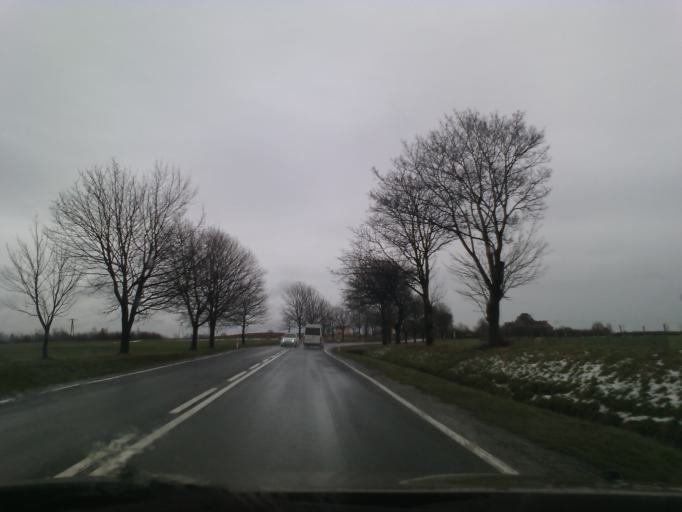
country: PL
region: Lower Silesian Voivodeship
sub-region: Powiat swidnicki
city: Swiebodzice
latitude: 50.8537
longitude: 16.3621
